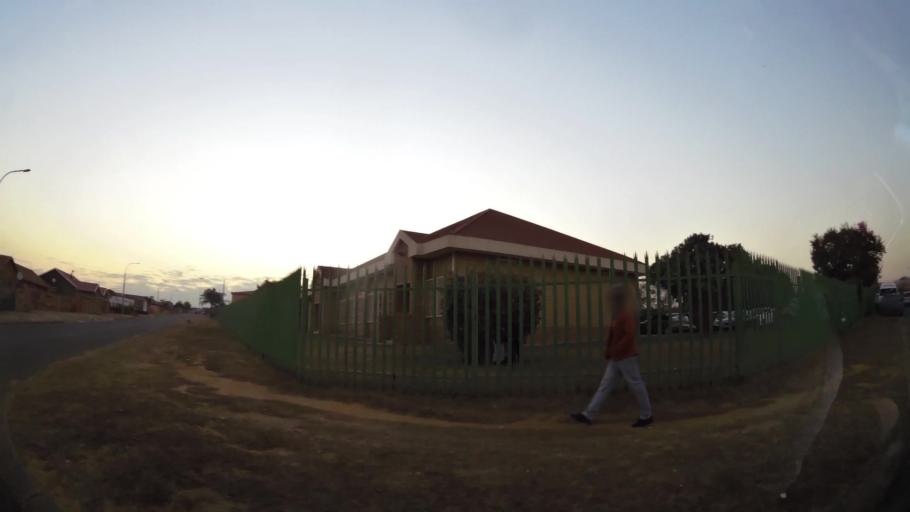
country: ZA
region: Gauteng
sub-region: West Rand District Municipality
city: Randfontein
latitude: -26.2113
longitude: 27.7136
